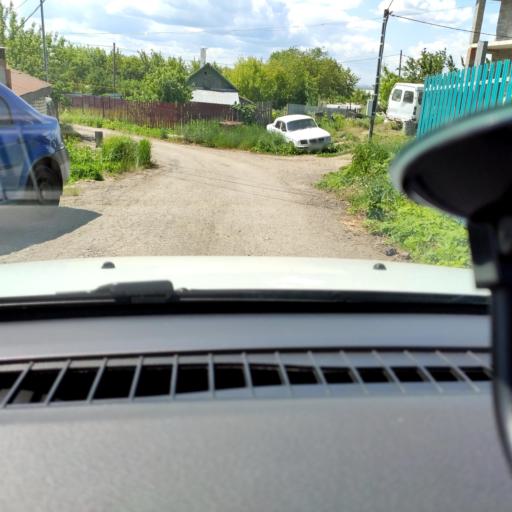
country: RU
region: Samara
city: Samara
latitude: 53.1756
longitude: 50.1632
